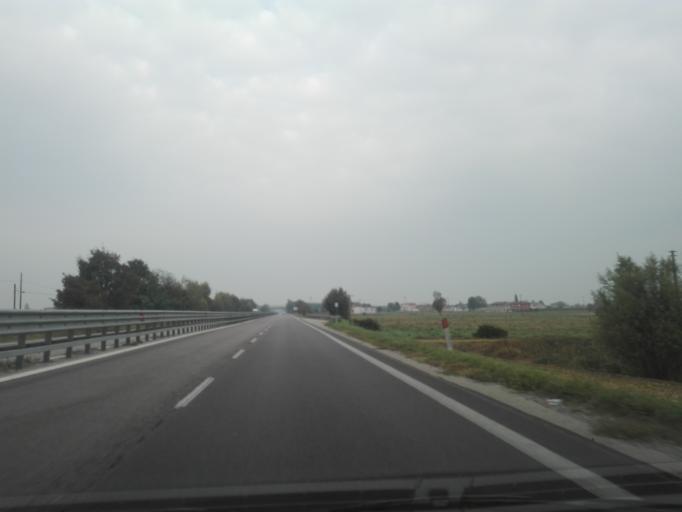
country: IT
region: Veneto
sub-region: Provincia di Verona
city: Spinimbecco
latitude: 45.1342
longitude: 11.3667
